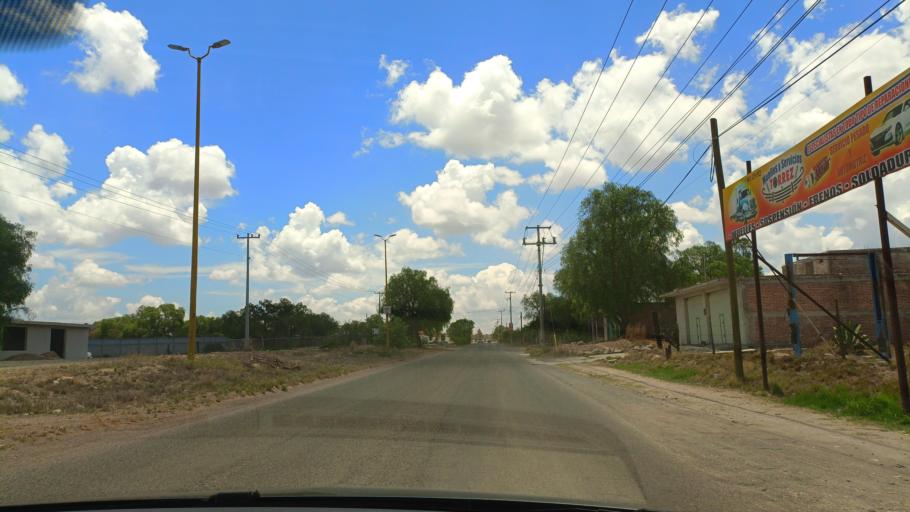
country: MX
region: Guanajuato
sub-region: San Luis de la Paz
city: San Ignacio
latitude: 21.2876
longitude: -100.5445
